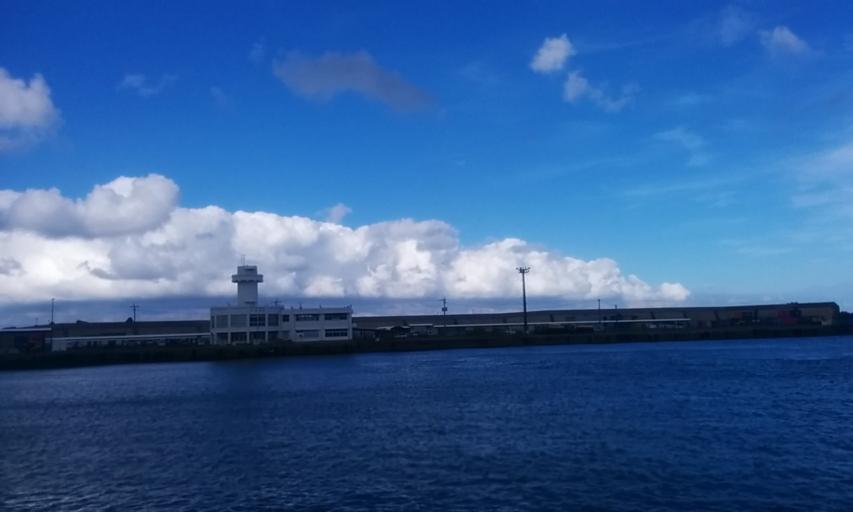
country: JP
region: Kagoshima
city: Nishinoomote
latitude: 30.4308
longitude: 130.5716
